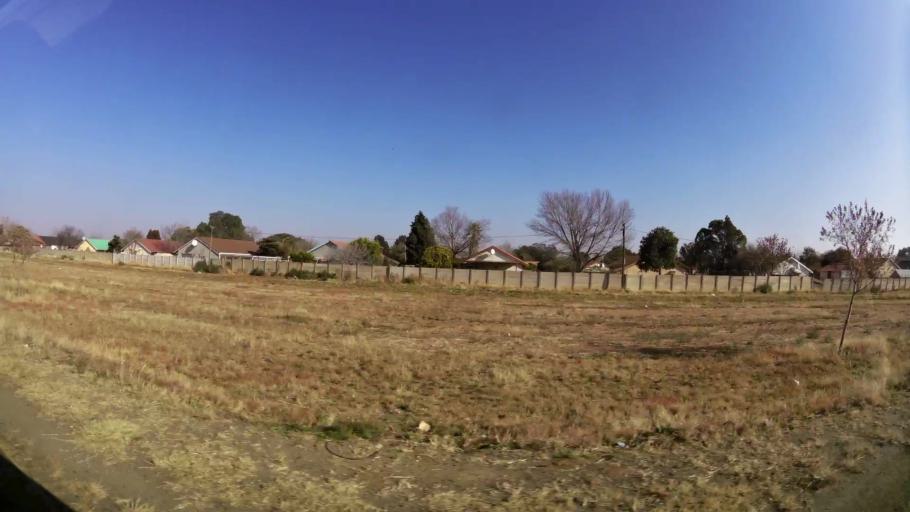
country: ZA
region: Orange Free State
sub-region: Mangaung Metropolitan Municipality
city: Bloemfontein
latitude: -29.1735
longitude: 26.1931
